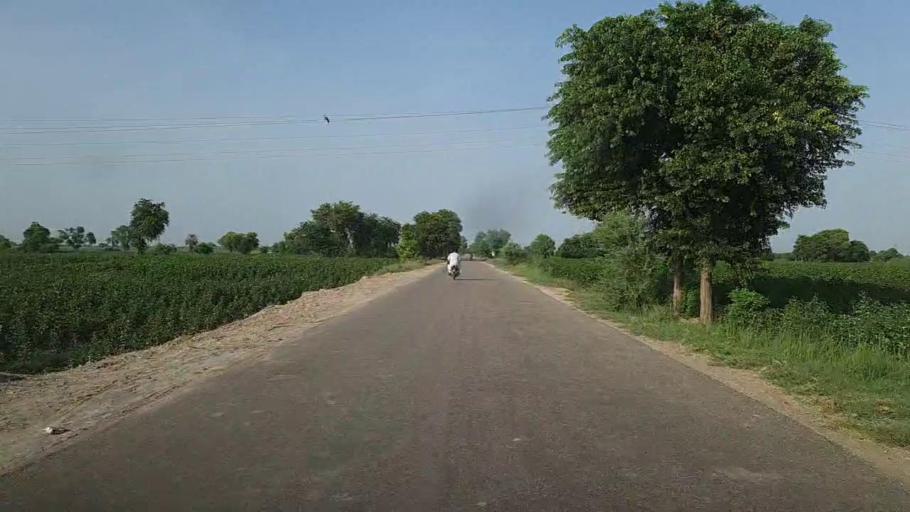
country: PK
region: Sindh
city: Khairpur
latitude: 28.0758
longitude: 69.8295
